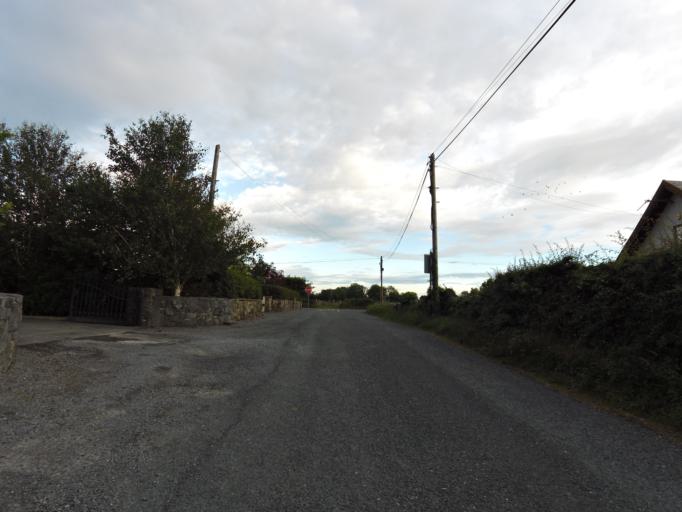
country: IE
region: Connaught
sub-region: County Galway
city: Athenry
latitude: 53.2880
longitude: -8.7128
